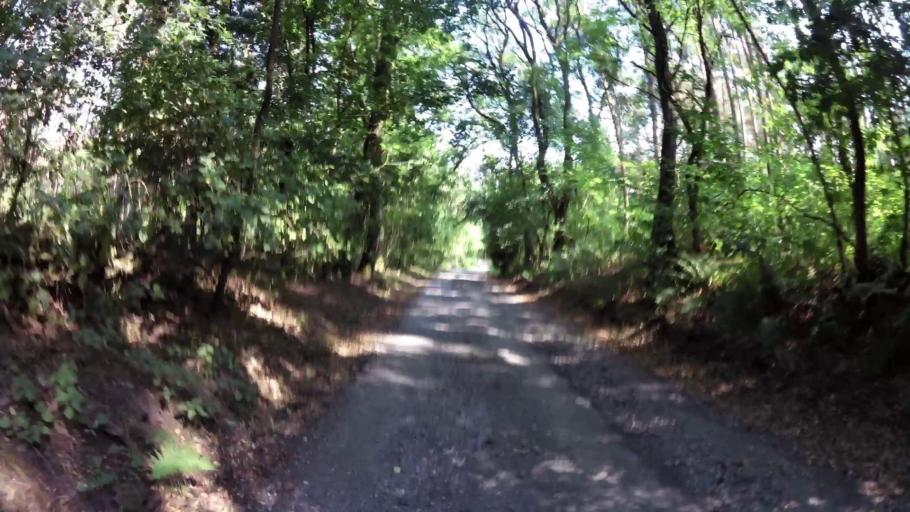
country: PL
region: West Pomeranian Voivodeship
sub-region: Powiat gryfinski
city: Moryn
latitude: 52.8729
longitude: 14.4156
